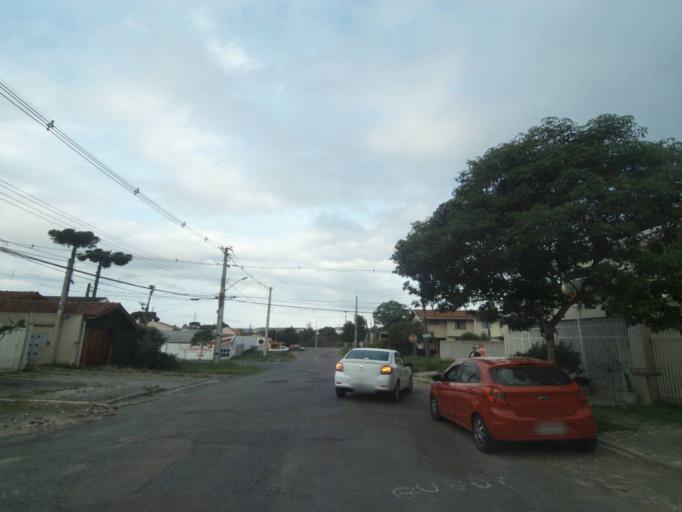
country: BR
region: Parana
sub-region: Pinhais
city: Pinhais
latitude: -25.4133
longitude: -49.1999
